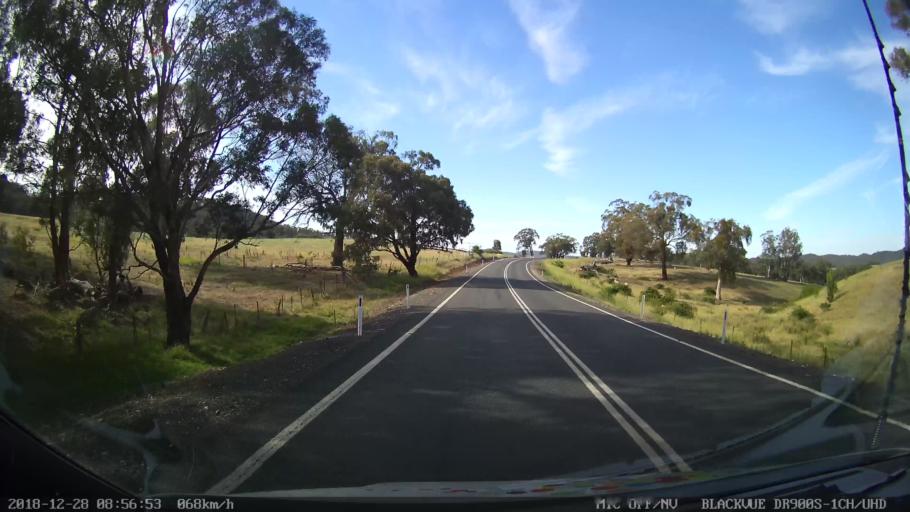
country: AU
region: New South Wales
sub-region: Upper Lachlan Shire
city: Crookwell
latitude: -34.1146
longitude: 149.3381
